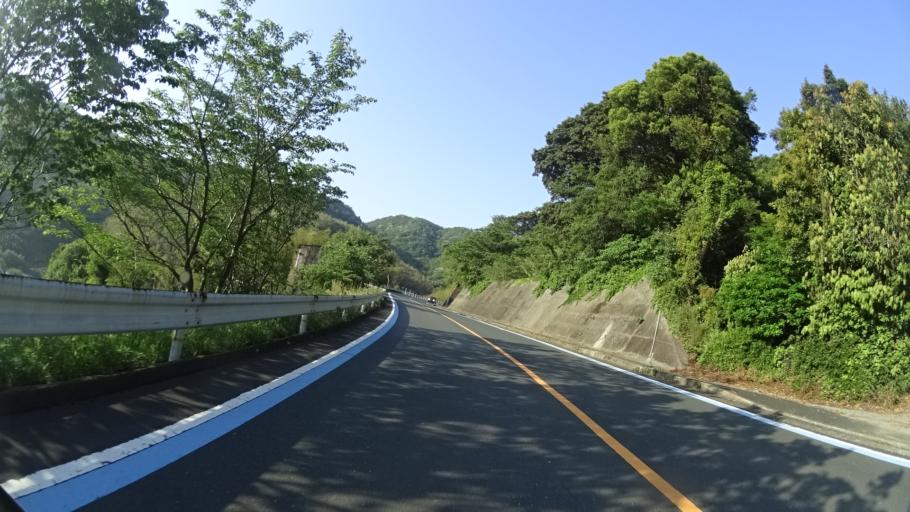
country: JP
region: Ehime
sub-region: Nishiuwa-gun
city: Ikata-cho
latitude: 33.4846
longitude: 132.3348
